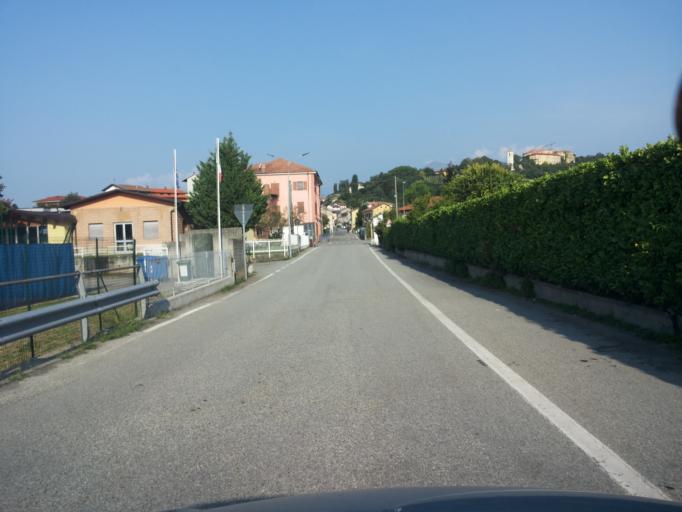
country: IT
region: Piedmont
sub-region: Provincia di Torino
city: Bollengo
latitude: 45.4704
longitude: 7.9494
